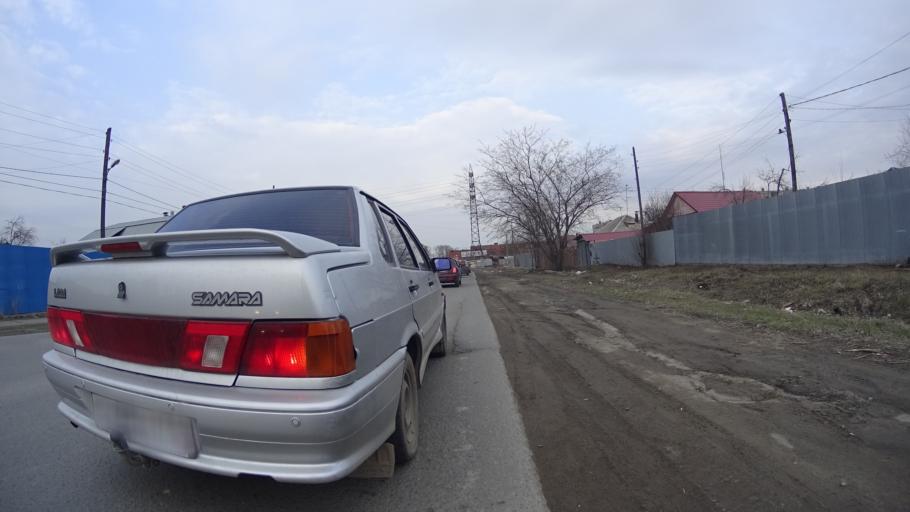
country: RU
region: Chelyabinsk
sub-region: Gorod Chelyabinsk
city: Chelyabinsk
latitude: 55.1903
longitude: 61.4798
